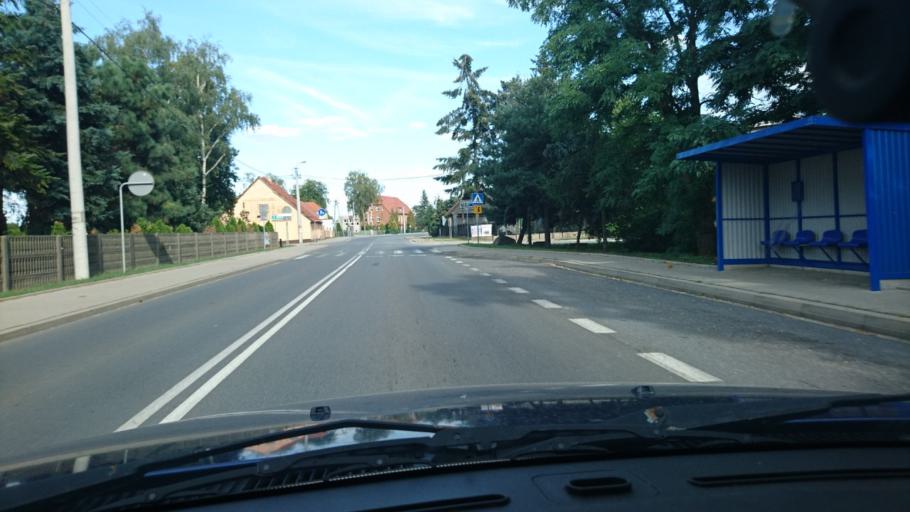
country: PL
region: Greater Poland Voivodeship
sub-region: Powiat krotoszynski
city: Krotoszyn
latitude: 51.7174
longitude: 17.3756
